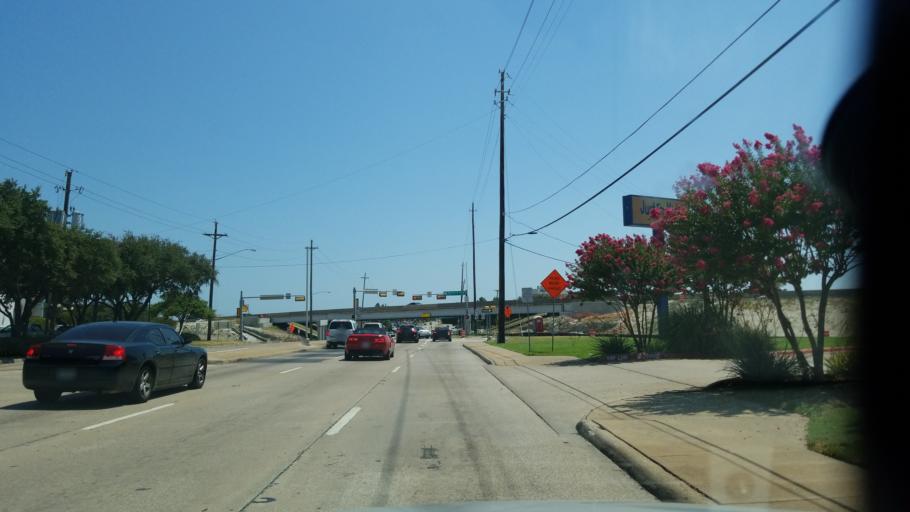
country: US
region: Texas
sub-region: Dallas County
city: Duncanville
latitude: 32.6474
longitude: -96.8864
